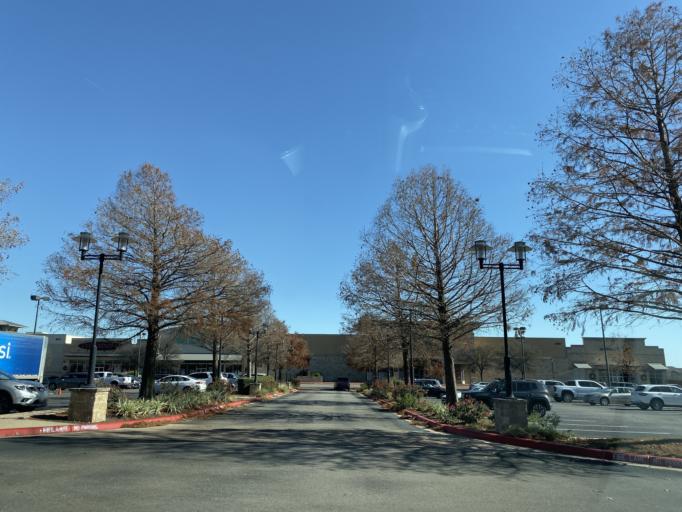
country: US
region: Texas
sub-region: Travis County
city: Windemere
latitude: 30.4775
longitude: -97.6699
